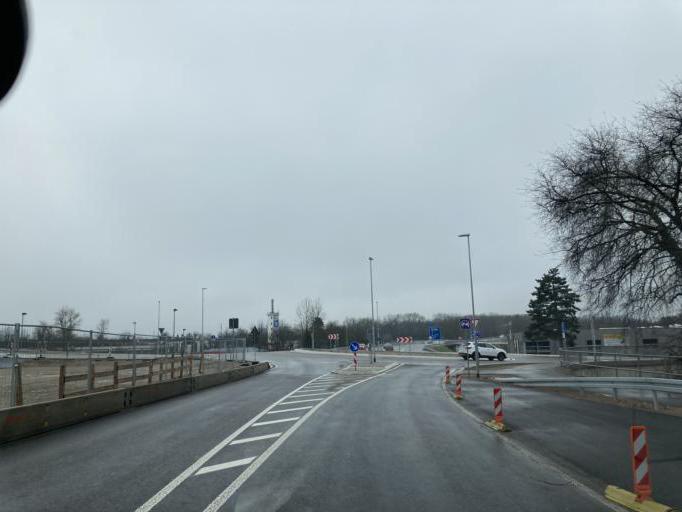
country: DE
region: Baden-Wuerttemberg
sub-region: Freiburg Region
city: Neuenburg am Rhein
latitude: 47.8152
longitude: 7.5579
